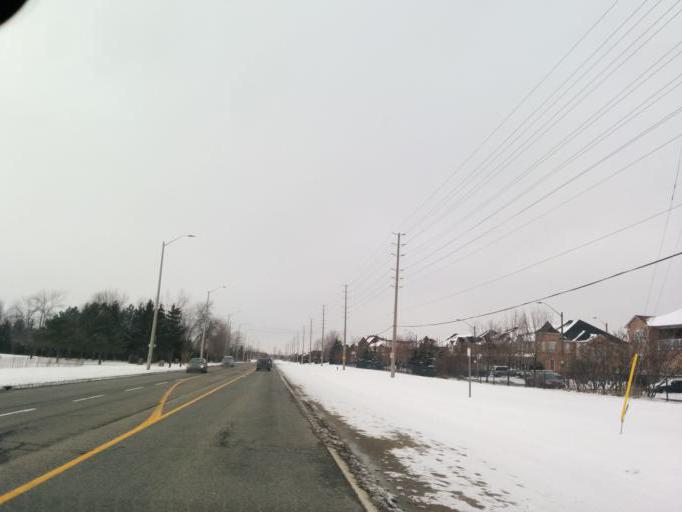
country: CA
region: Ontario
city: Mississauga
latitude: 43.5444
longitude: -79.7458
